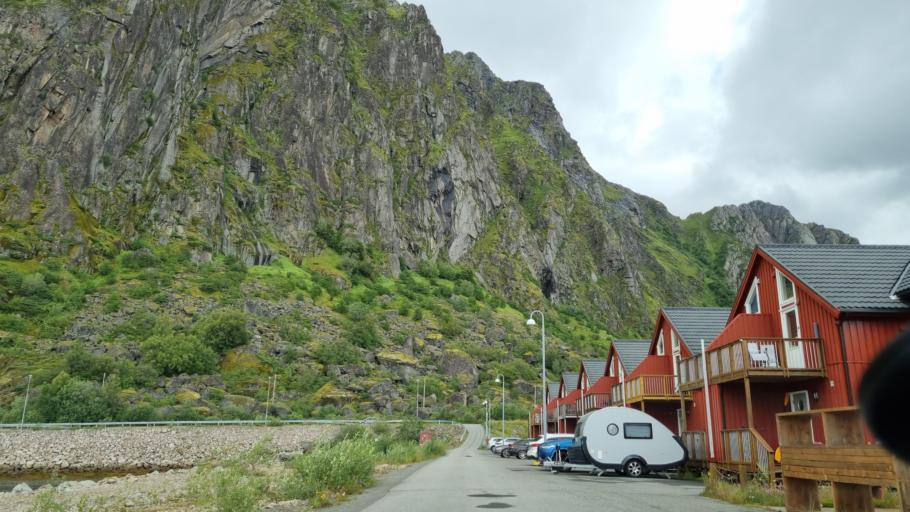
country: NO
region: Nordland
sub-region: Vagan
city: Svolvaer
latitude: 68.2408
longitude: 14.5906
